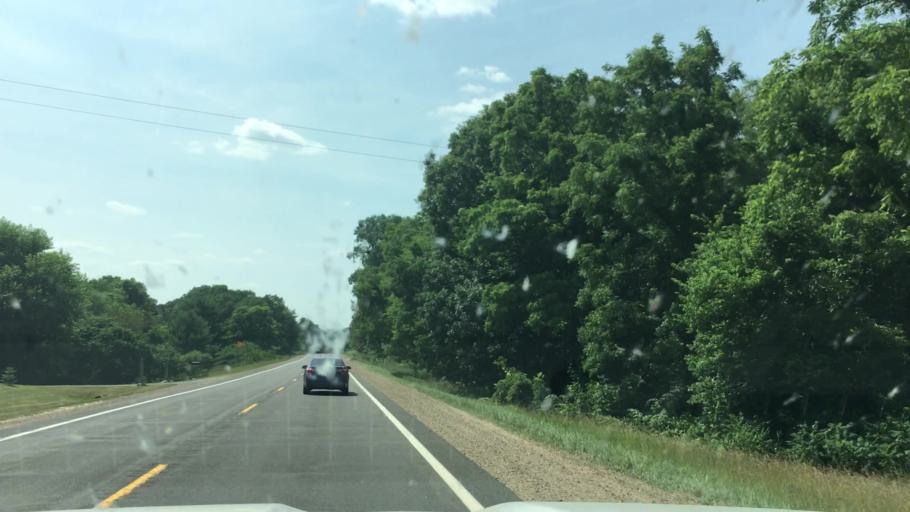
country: US
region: Michigan
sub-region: Allegan County
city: Plainwell
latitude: 42.4346
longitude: -85.5643
